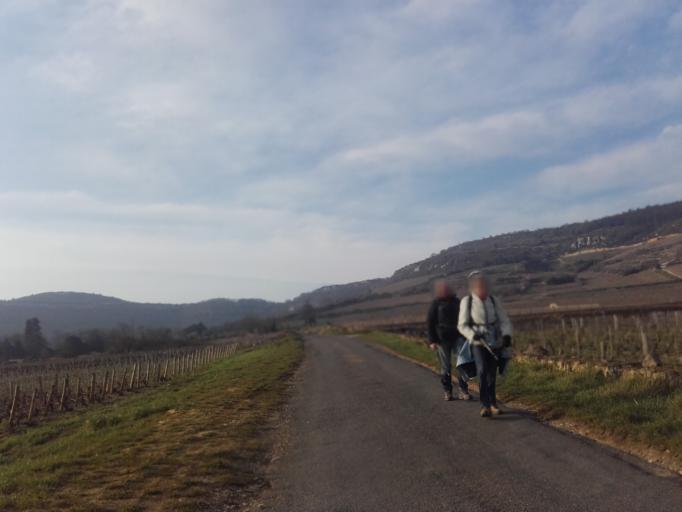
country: FR
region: Bourgogne
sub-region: Departement de Saone-et-Loire
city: Chagny
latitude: 46.9121
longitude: 4.6902
